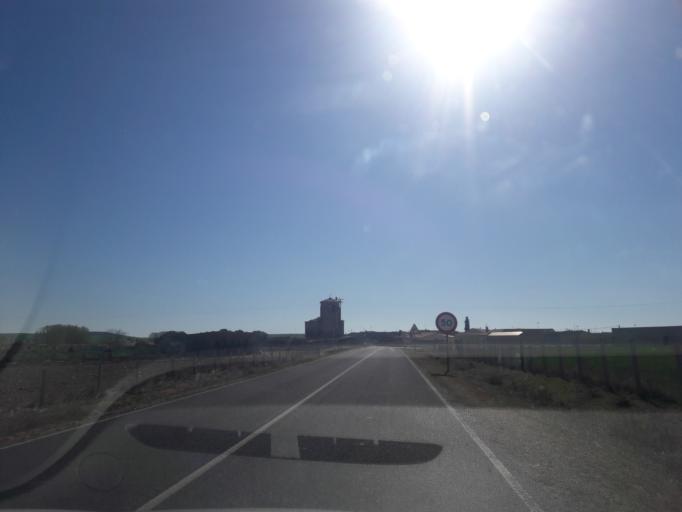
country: ES
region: Castille and Leon
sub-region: Provincia de Salamanca
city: Salmoral
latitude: 40.8026
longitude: -5.2236
